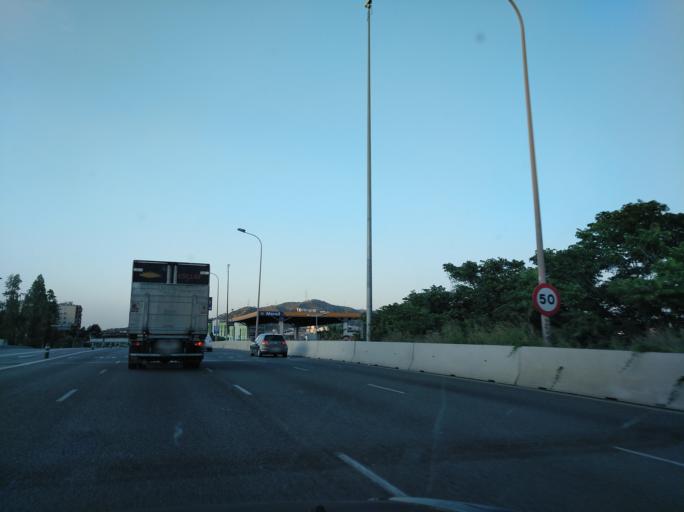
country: ES
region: Catalonia
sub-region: Provincia de Barcelona
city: Sant Andreu de Palomar
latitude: 41.4467
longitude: 2.1878
